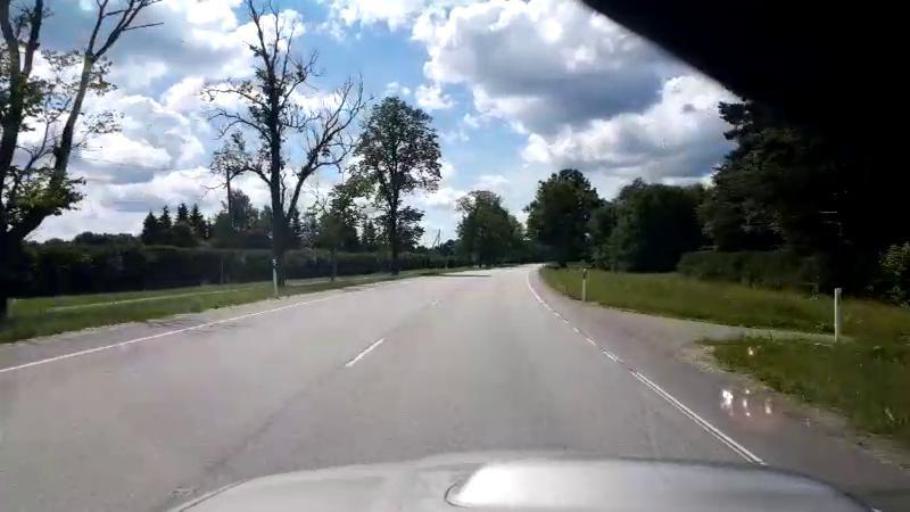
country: EE
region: Jaervamaa
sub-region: Jaerva-Jaani vald
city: Jarva-Jaani
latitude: 59.0382
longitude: 25.7078
